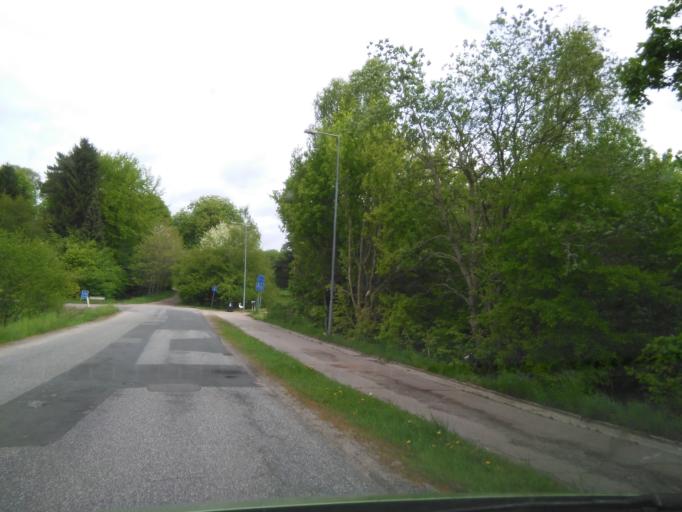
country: DK
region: Central Jutland
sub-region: Skanderborg Kommune
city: Skanderborg
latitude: 56.0669
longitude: 9.8542
